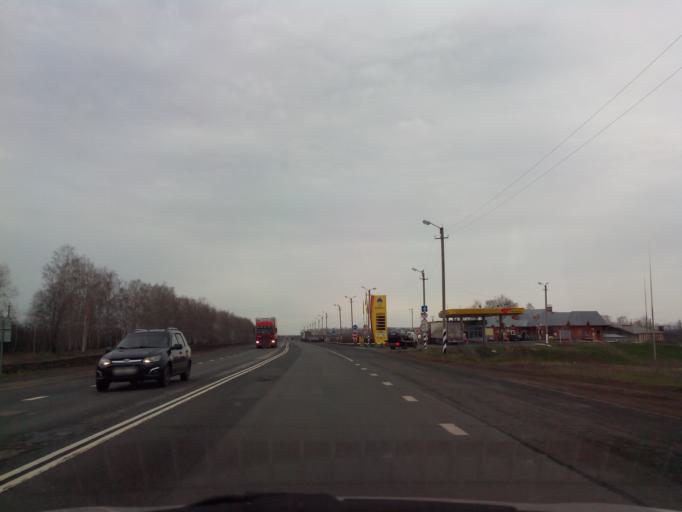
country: RU
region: Tambov
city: Zavoronezhskoye
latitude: 52.9762
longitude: 40.5683
